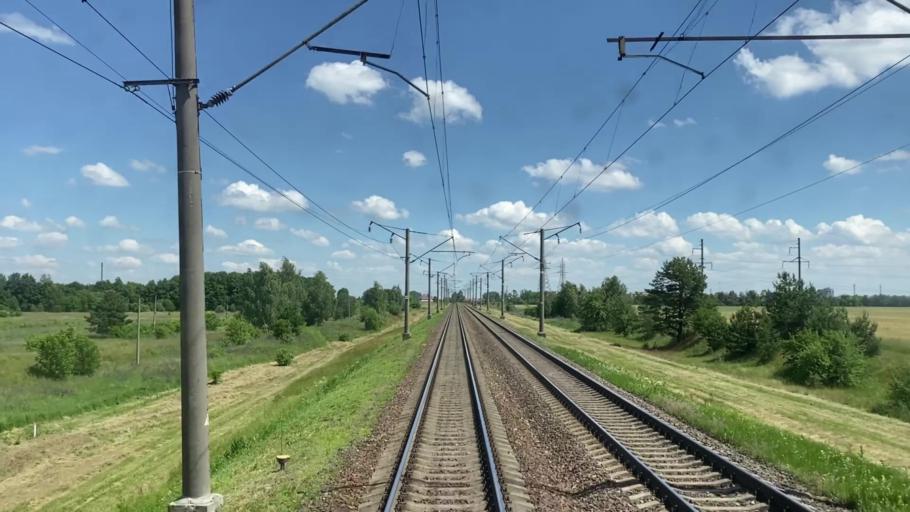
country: BY
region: Brest
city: Baranovichi
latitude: 53.0993
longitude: 25.9472
